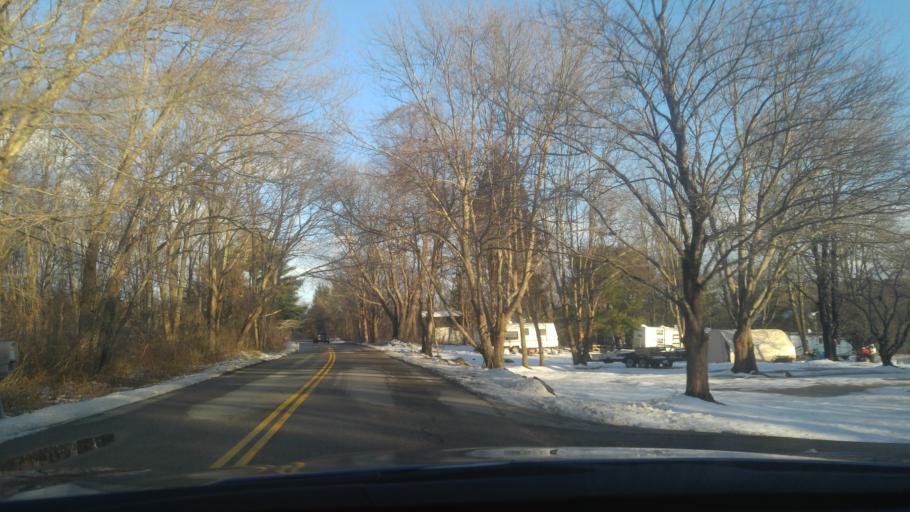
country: US
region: Rhode Island
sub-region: Kent County
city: Coventry
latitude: 41.7193
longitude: -71.6617
